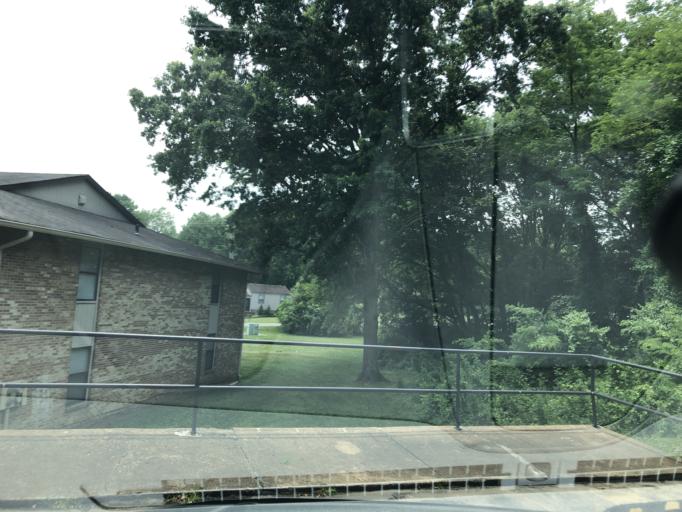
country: US
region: Tennessee
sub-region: Davidson County
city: Oak Hill
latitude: 36.0650
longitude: -86.6923
